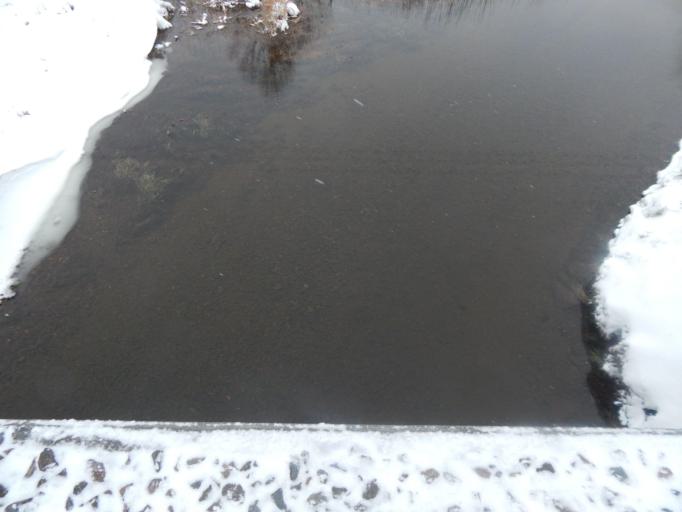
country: BY
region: Minsk
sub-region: Minski Rayon
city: Krasnaye
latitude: 54.1304
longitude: 27.1079
